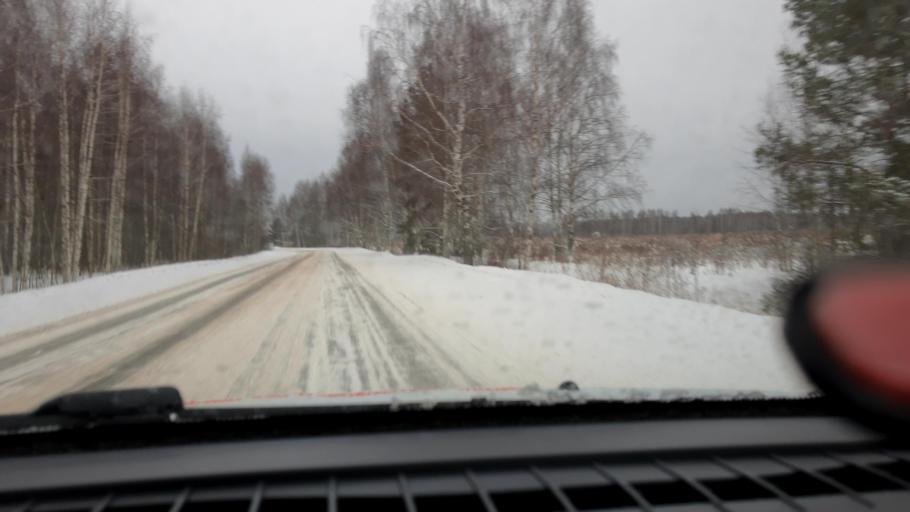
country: RU
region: Nizjnij Novgorod
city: Pamyat' Parizhskoy Kommuny
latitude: 56.2638
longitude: 44.4417
